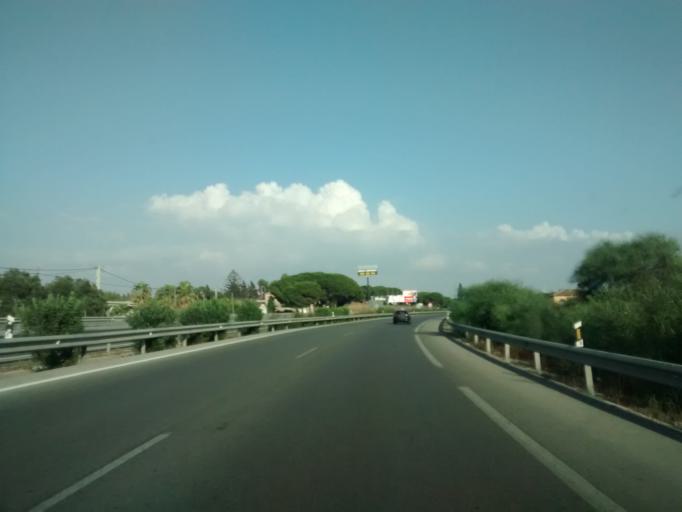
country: ES
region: Andalusia
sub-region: Provincia de Cadiz
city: Chiclana de la Frontera
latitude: 36.4441
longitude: -6.1380
